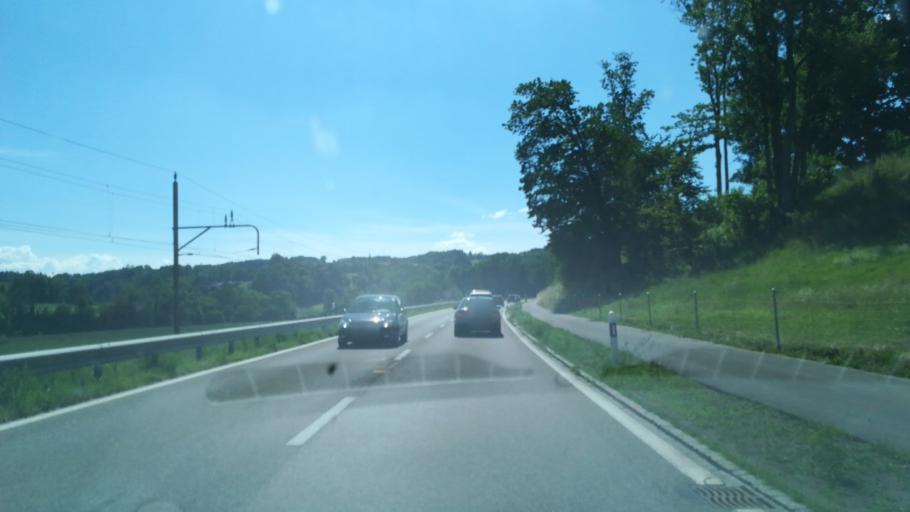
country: CH
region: Saint Gallen
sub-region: Wahlkreis Wil
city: Niederburen
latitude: 47.4979
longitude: 9.2264
